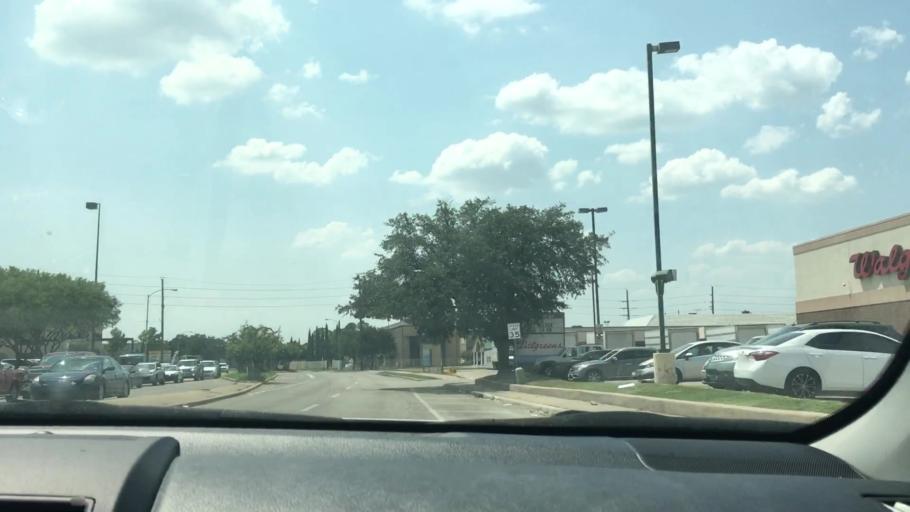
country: US
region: Texas
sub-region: Fort Bend County
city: Mission Bend
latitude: 29.7041
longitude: -95.6446
